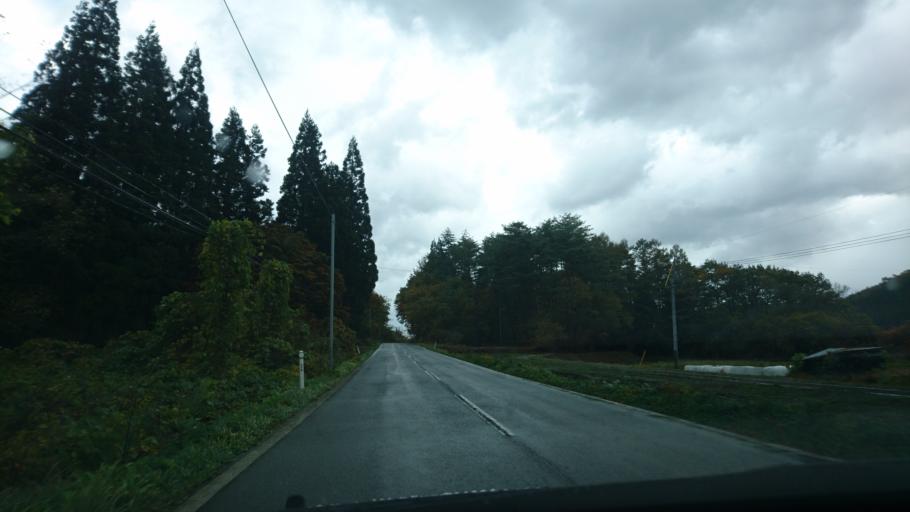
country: JP
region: Iwate
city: Shizukuishi
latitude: 39.6187
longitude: 140.9457
